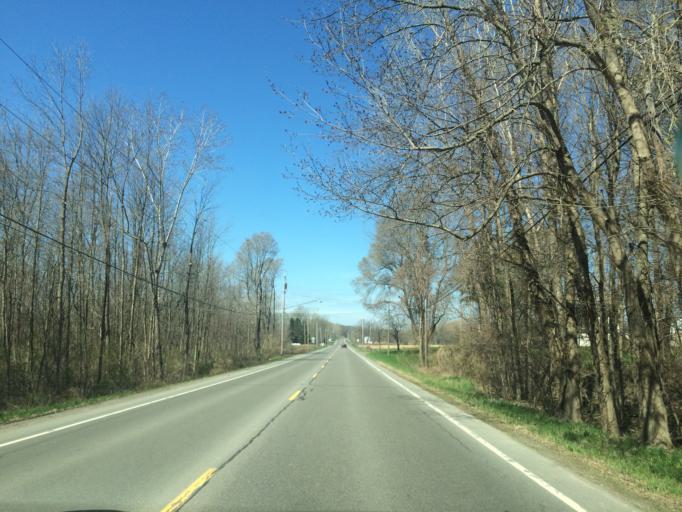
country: US
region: New York
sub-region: Wayne County
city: Macedon
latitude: 43.0942
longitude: -77.3293
